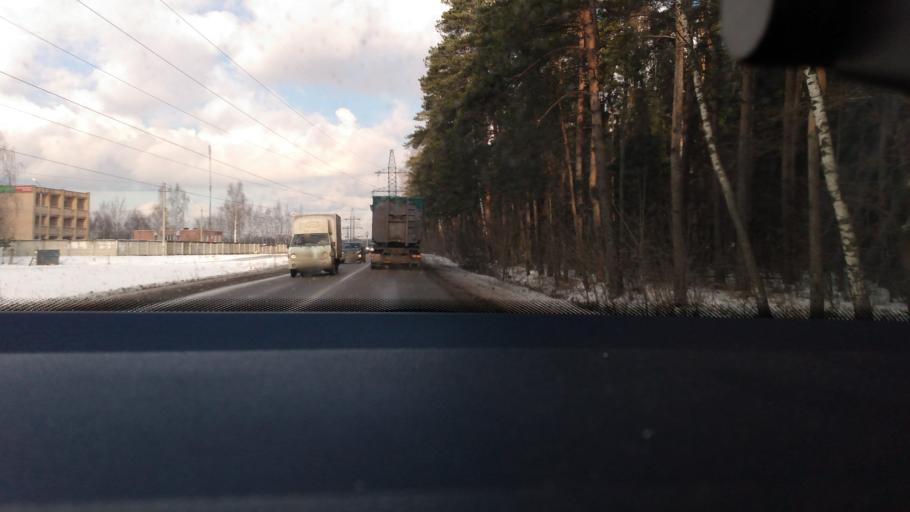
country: RU
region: Moskovskaya
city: Rodniki
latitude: 55.6866
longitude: 38.0816
